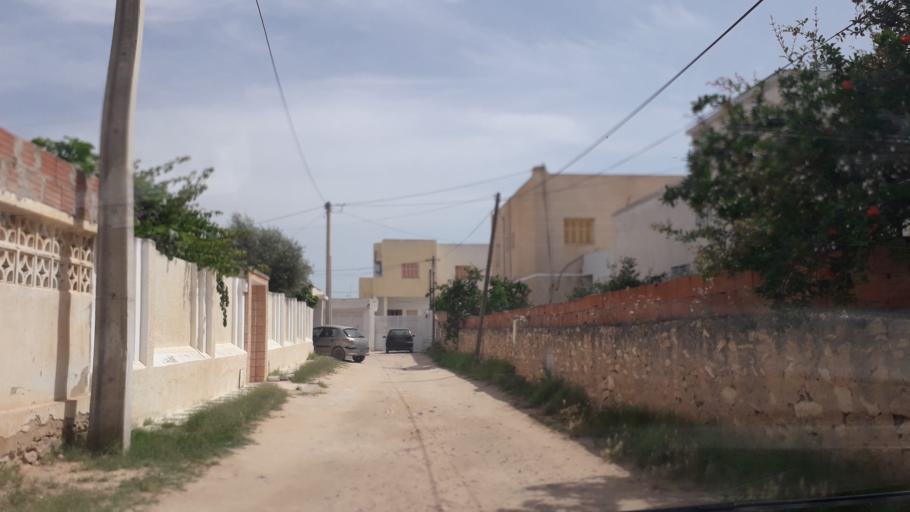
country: TN
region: Safaqis
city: Al Qarmadah
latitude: 34.8006
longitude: 10.7695
